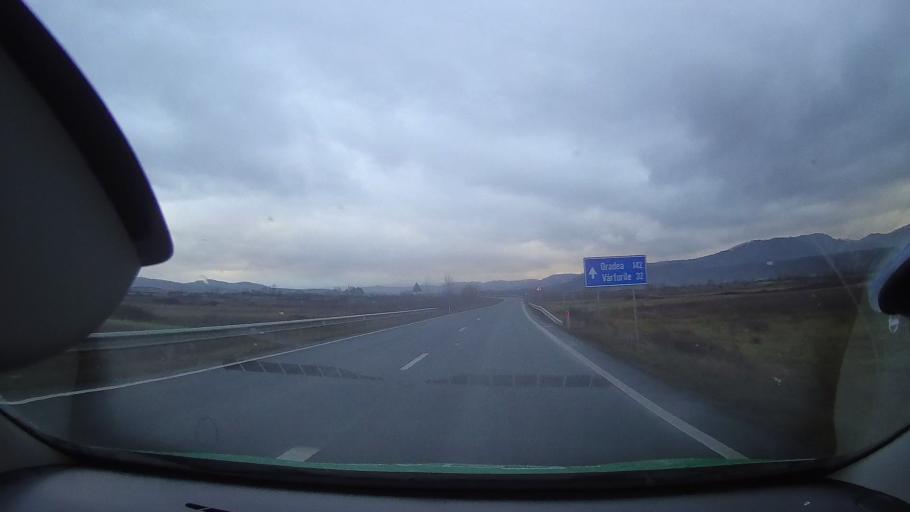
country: RO
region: Hunedoara
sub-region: Comuna Ribita
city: Ribita
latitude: 46.1668
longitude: 22.7485
